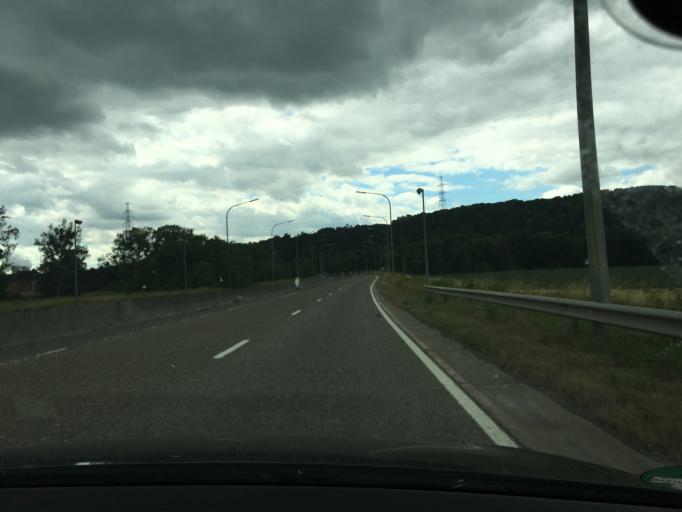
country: BE
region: Wallonia
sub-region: Province de Liege
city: Amay
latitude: 50.5552
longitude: 5.3433
